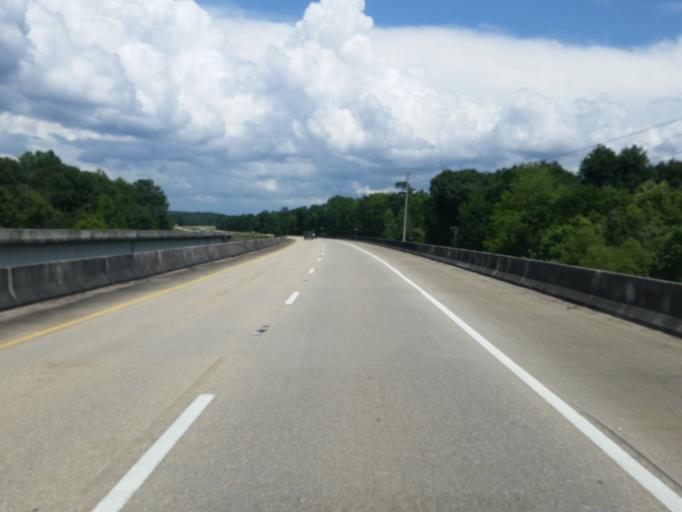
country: US
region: Mississippi
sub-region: Perry County
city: New Augusta
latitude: 31.1075
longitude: -88.8082
